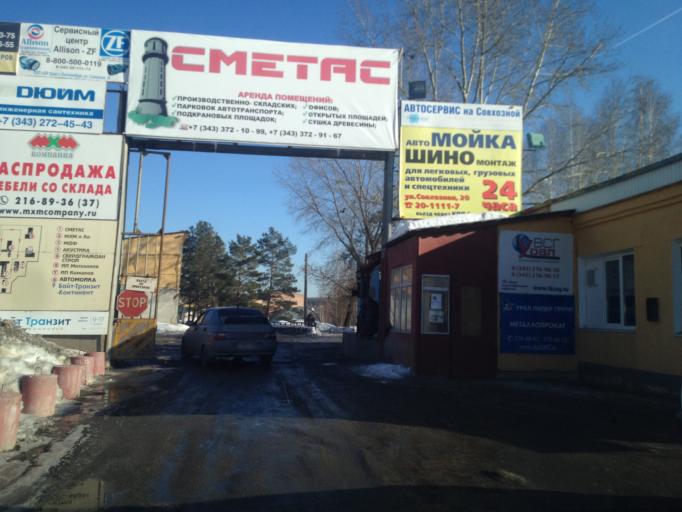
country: RU
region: Sverdlovsk
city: Yekaterinburg
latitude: 56.9119
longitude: 60.6294
